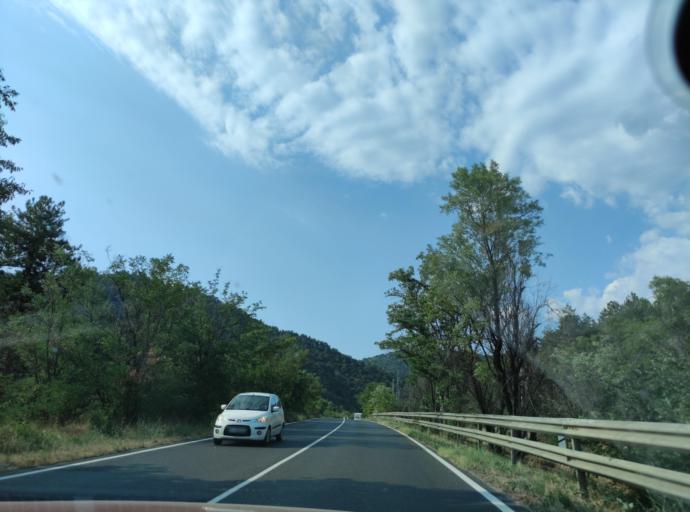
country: BG
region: Blagoevgrad
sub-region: Obshtina Kresna
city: Kresna
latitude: 41.7381
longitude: 23.1590
